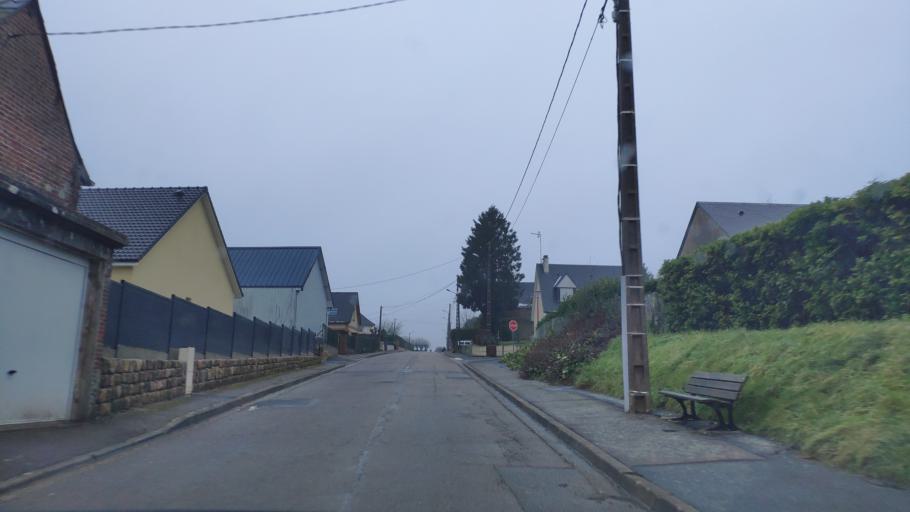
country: FR
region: Haute-Normandie
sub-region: Departement de la Seine-Maritime
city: Doudeville
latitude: 49.7227
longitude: 0.7839
